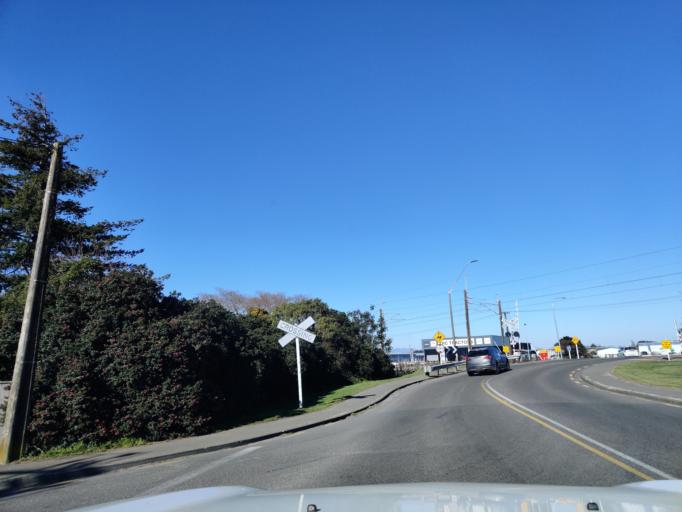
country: NZ
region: Manawatu-Wanganui
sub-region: Palmerston North City
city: Palmerston North
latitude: -40.2320
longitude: 175.5741
